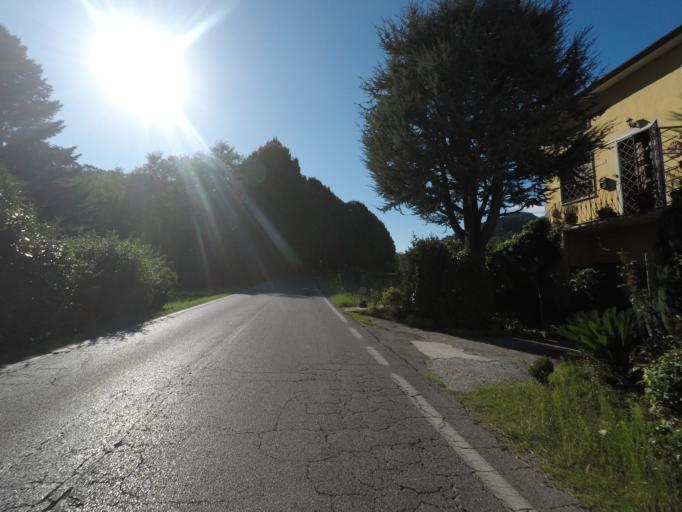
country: IT
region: Tuscany
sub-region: Provincia di Lucca
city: San Martino in Freddana-Monsagrati
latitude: 43.8986
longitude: 10.3898
